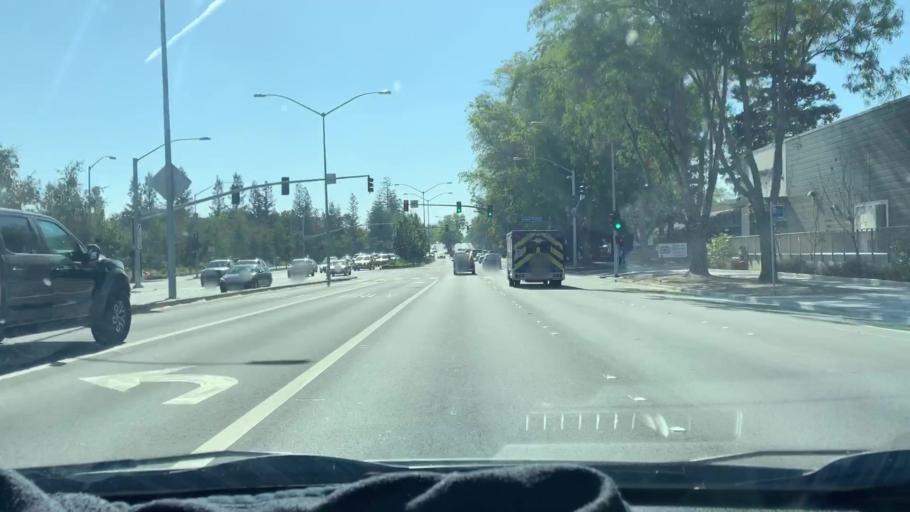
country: US
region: California
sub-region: Santa Clara County
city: Cupertino
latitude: 37.3356
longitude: -122.0143
